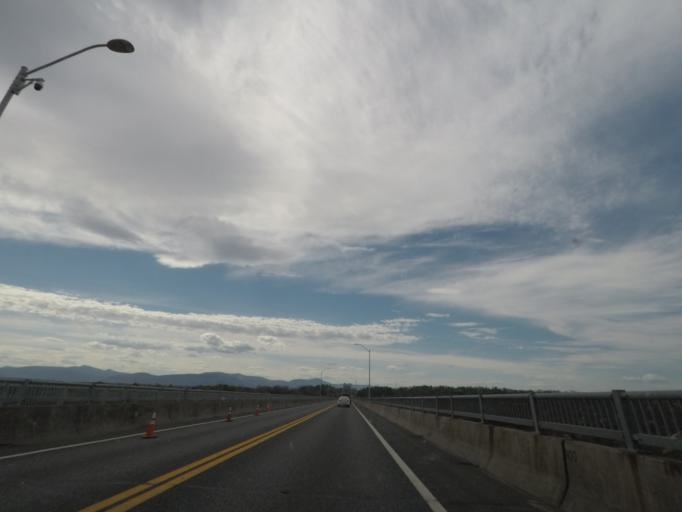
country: US
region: New York
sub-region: Greene County
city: Catskill
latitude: 42.2217
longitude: -73.8434
